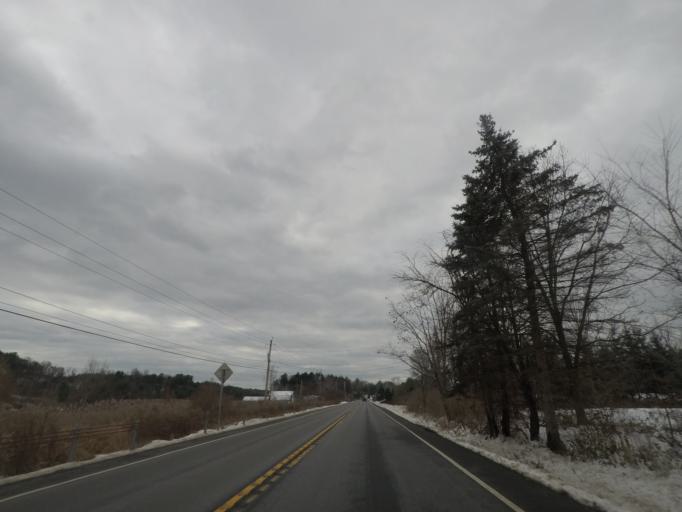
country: US
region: New York
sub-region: Rensselaer County
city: West Sand Lake
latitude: 42.6234
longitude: -73.6035
